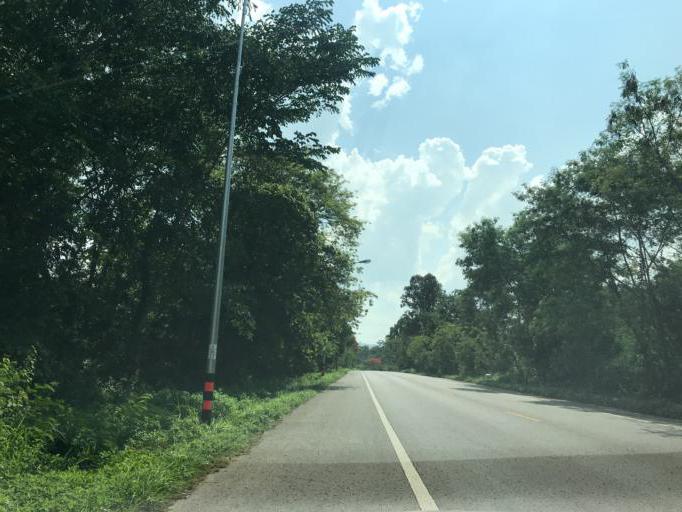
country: TH
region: Phayao
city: Phayao
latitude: 19.0853
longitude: 99.8869
